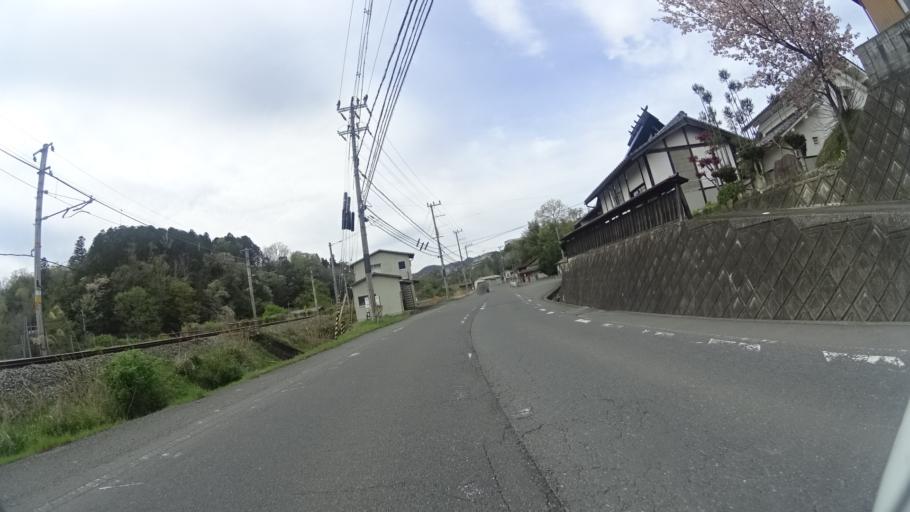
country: JP
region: Kyoto
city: Kameoka
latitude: 35.1757
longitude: 135.4921
